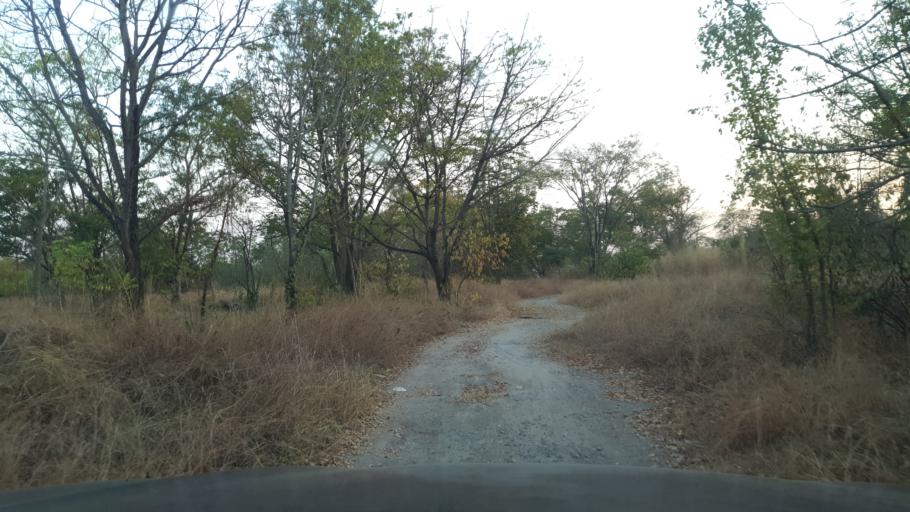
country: TH
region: Nakhon Sawan
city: Kao Liao
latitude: 15.7806
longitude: 99.9770
